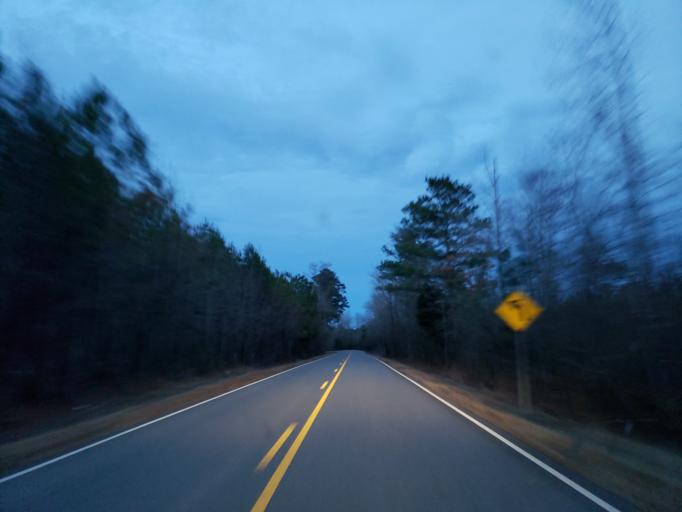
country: US
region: Alabama
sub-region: Greene County
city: Eutaw
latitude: 32.8870
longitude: -88.0479
